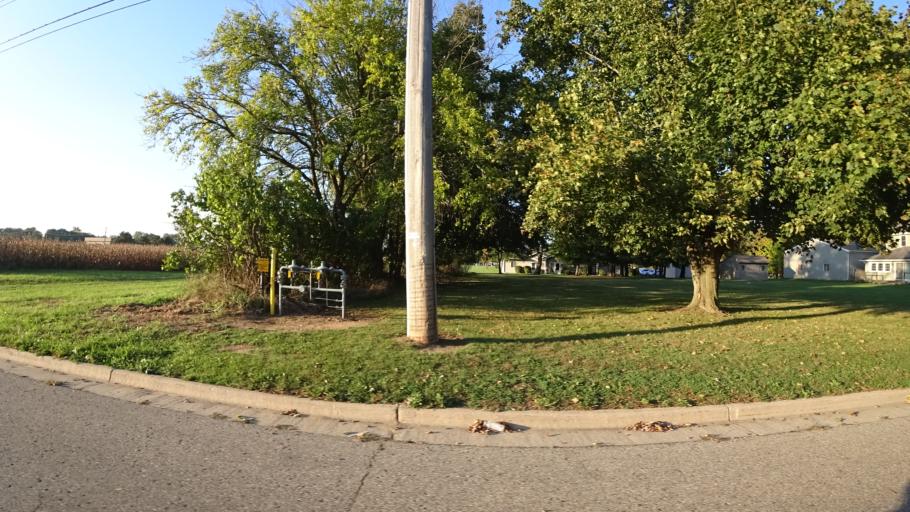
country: US
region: Michigan
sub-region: Saint Joseph County
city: Three Rivers
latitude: 41.9493
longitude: -85.6442
